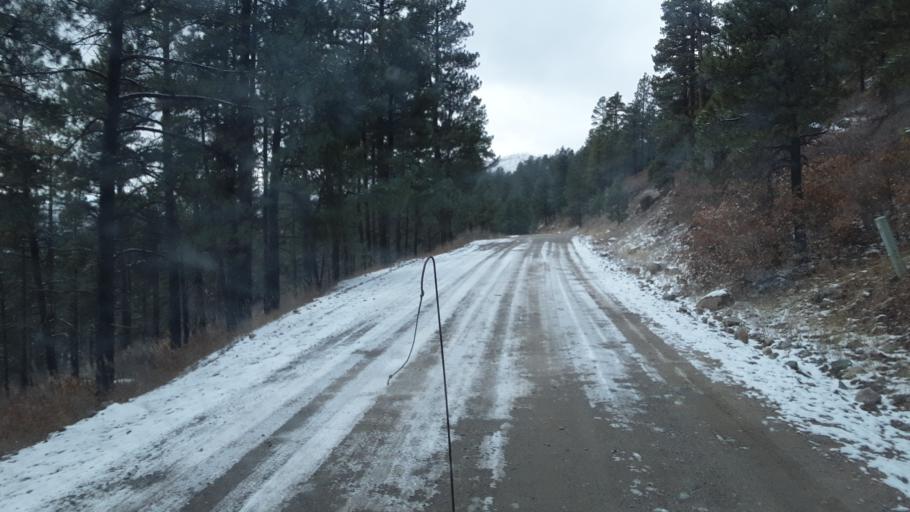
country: US
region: Colorado
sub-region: La Plata County
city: Bayfield
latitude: 37.4080
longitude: -107.5274
